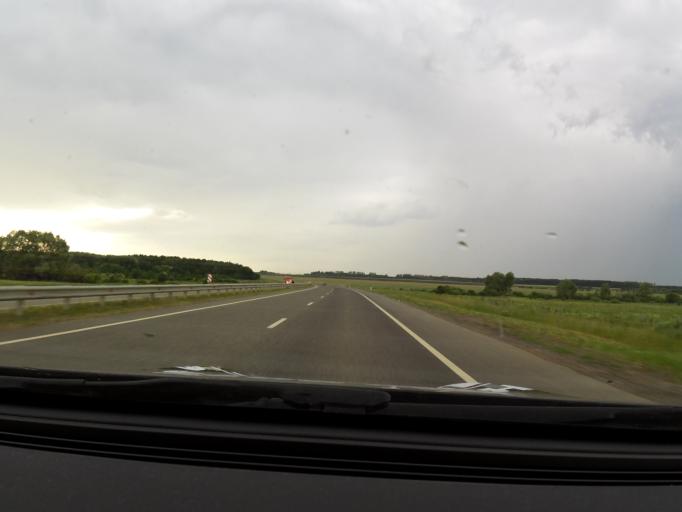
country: RU
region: Bashkortostan
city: Kushnarenkovo
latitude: 55.0674
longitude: 55.3529
